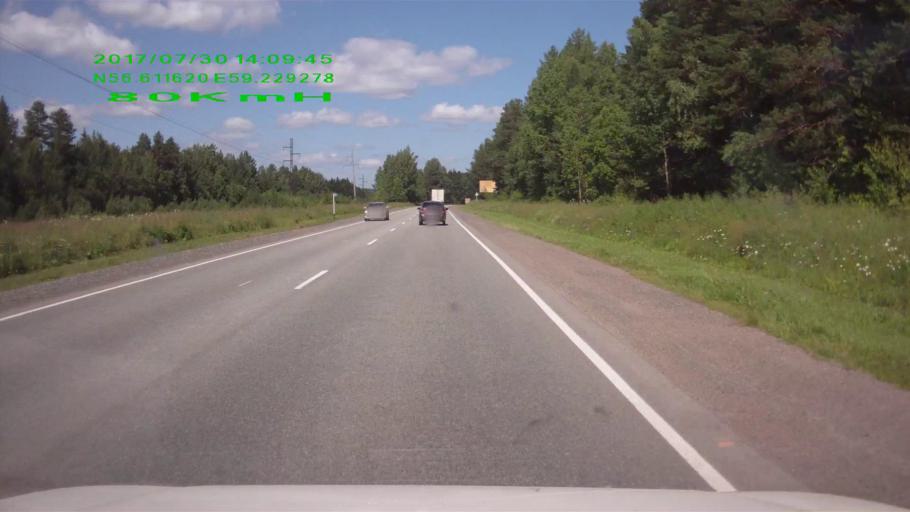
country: RU
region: Sverdlovsk
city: Nizhniye Sergi
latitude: 56.6118
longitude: 59.2294
